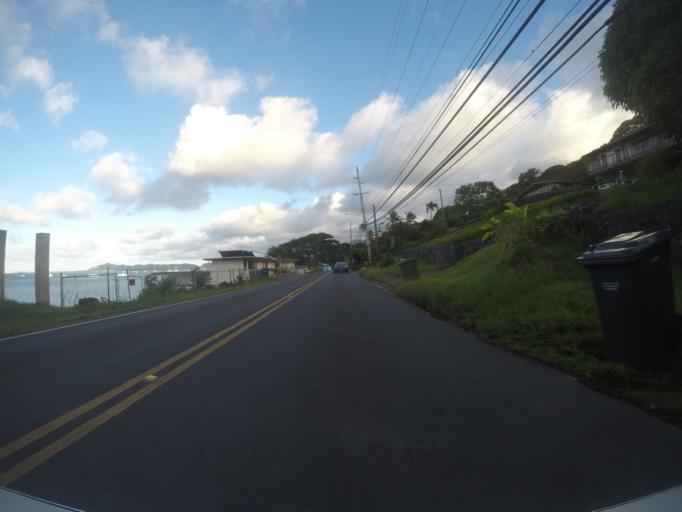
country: US
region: Hawaii
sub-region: Honolulu County
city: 'Ahuimanu
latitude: 21.4518
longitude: -157.8152
